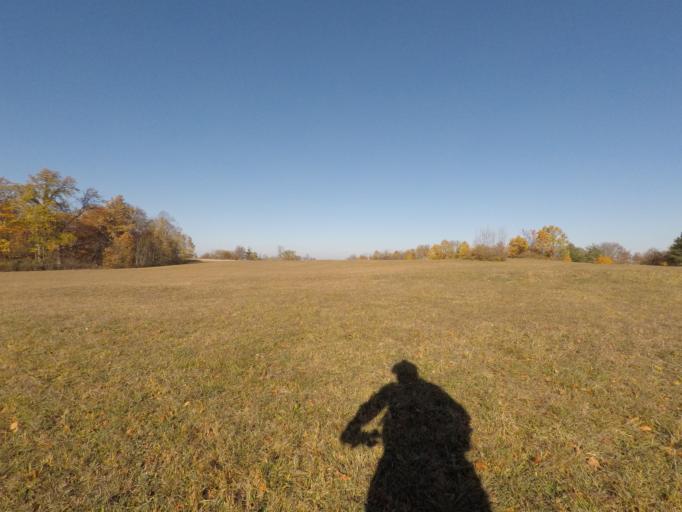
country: DE
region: Baden-Wuerttemberg
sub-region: Tuebingen Region
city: Pfullingen
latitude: 48.4401
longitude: 9.2258
